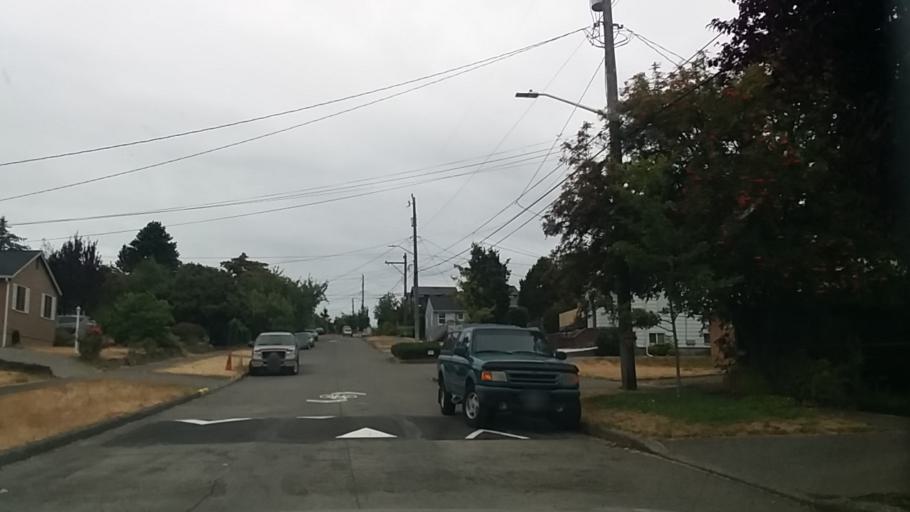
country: US
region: Washington
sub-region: King County
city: Shoreline
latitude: 47.6956
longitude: -122.3458
